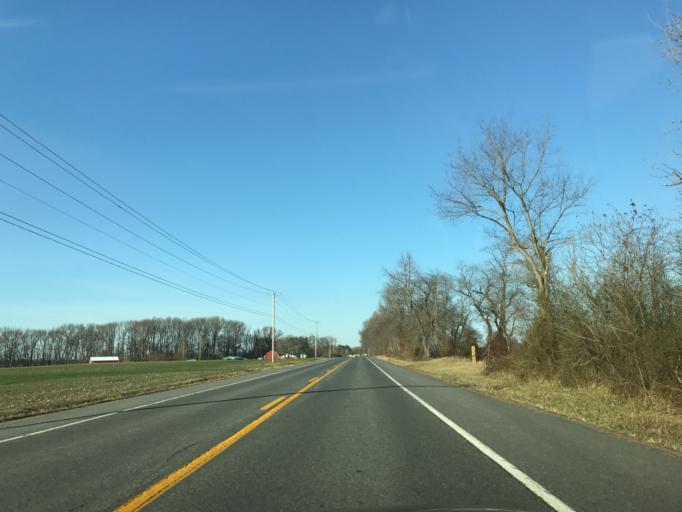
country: US
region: Maryland
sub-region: Queen Anne's County
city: Kingstown
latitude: 39.1712
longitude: -75.8596
